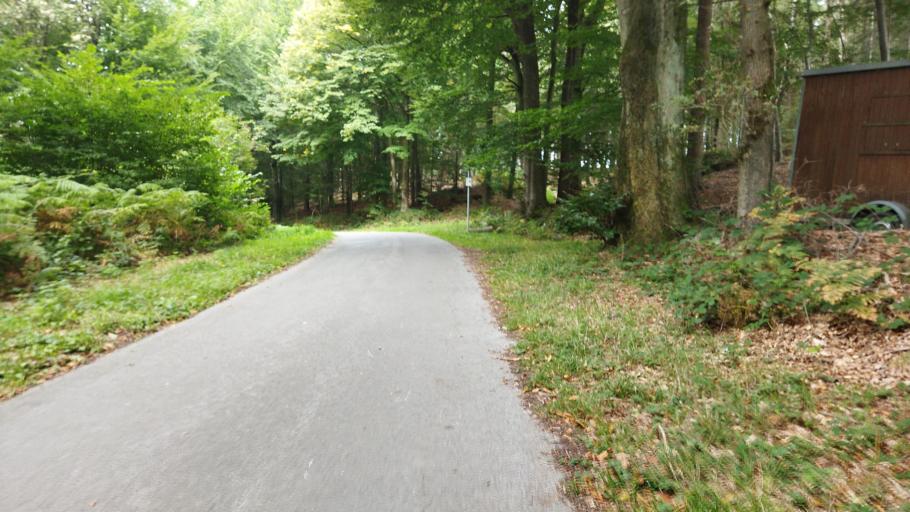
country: DE
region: Lower Saxony
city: Hilter
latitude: 52.1613
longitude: 8.1185
